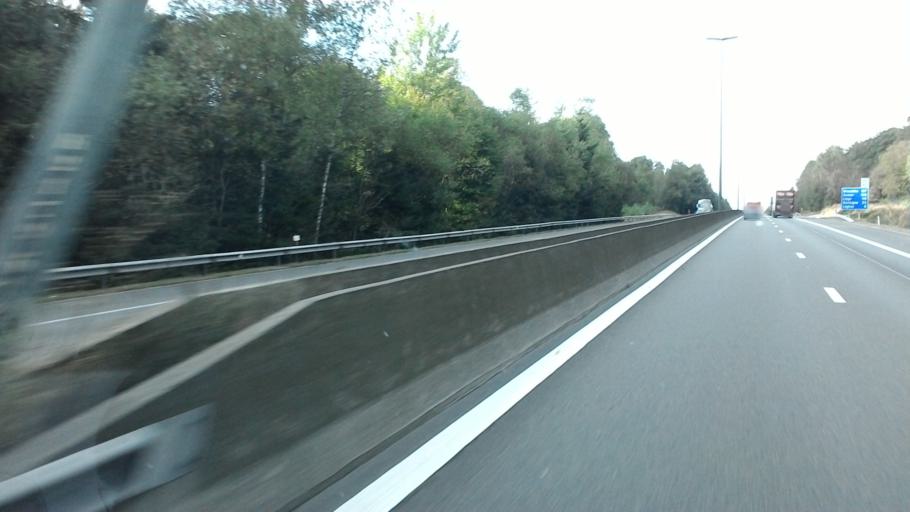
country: BE
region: Wallonia
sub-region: Province du Luxembourg
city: Leglise
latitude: 49.7546
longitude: 5.5654
